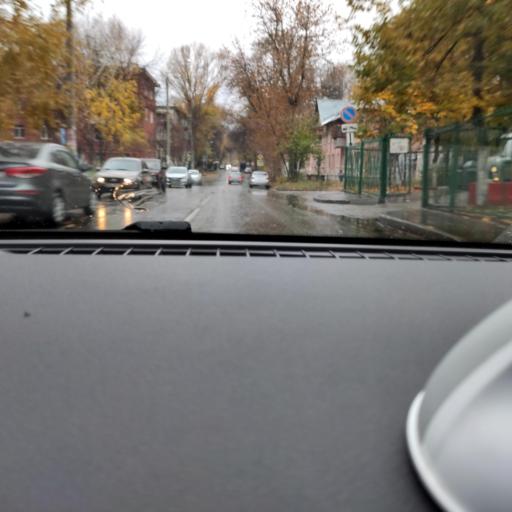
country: RU
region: Samara
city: Samara
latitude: 53.2287
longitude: 50.2595
